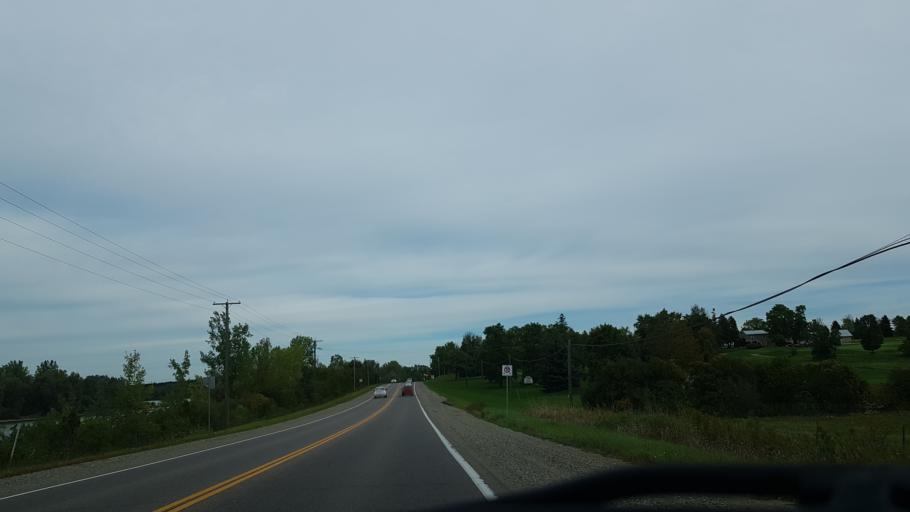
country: CA
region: Ontario
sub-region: Wellington County
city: Guelph
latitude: 43.5991
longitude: -80.2335
